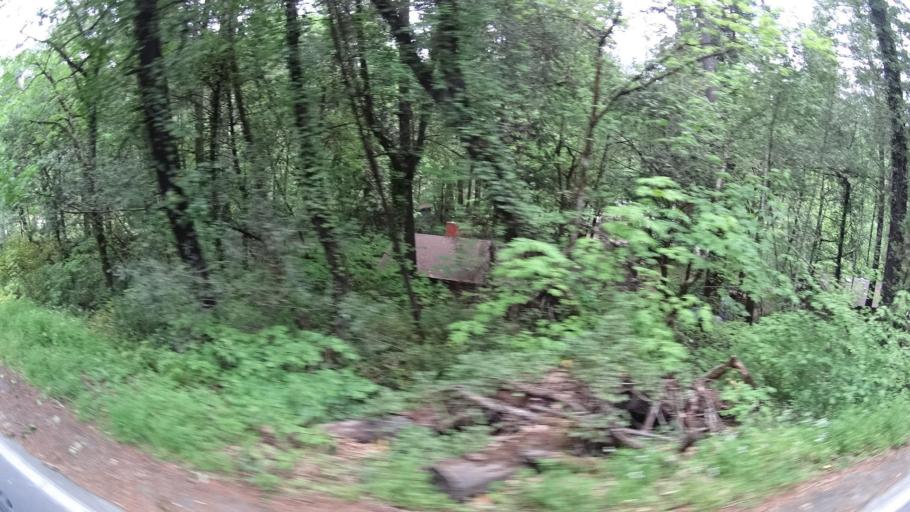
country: US
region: California
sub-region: Humboldt County
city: Redway
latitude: 40.1242
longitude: -123.8325
